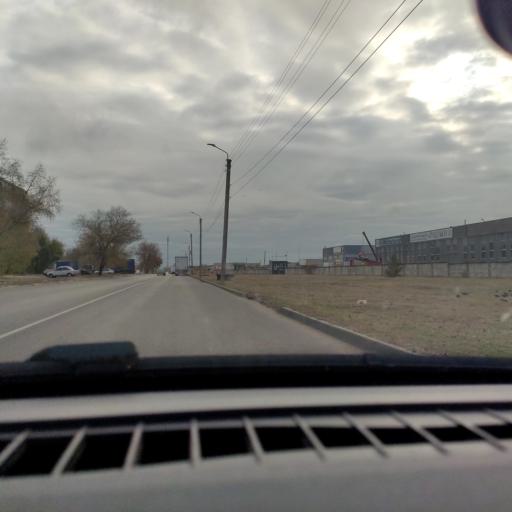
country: RU
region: Voronezj
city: Maslovka
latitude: 51.5970
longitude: 39.2368
